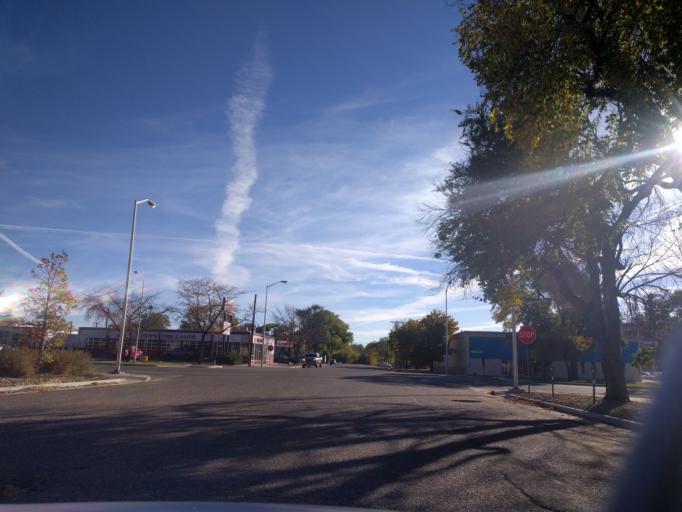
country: US
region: Colorado
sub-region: El Paso County
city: Colorado Springs
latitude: 38.8309
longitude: -104.8188
